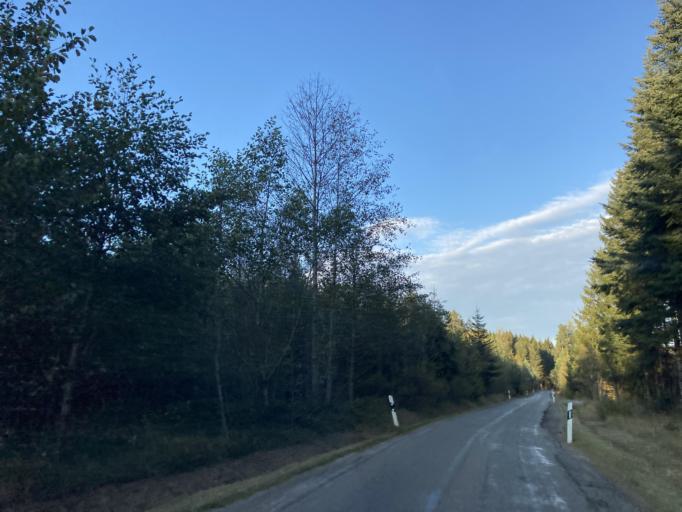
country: DE
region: Baden-Wuerttemberg
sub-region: Freiburg Region
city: Braunlingen
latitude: 47.9905
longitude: 8.3906
